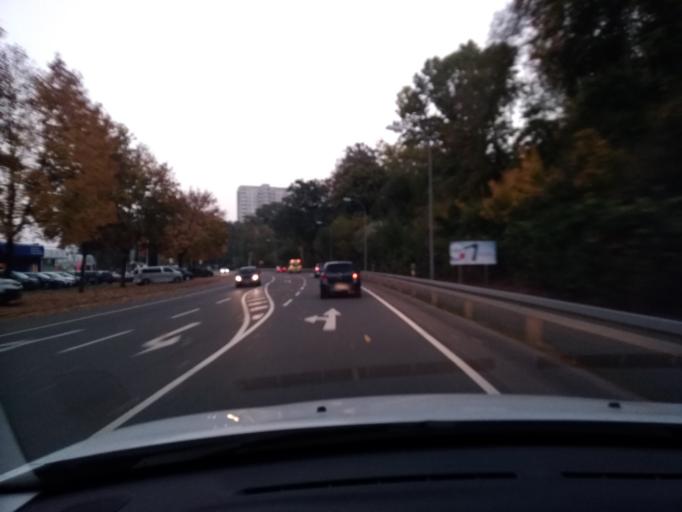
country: FR
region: Lorraine
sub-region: Departement de la Moselle
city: Alsting
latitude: 49.2004
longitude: 7.0164
